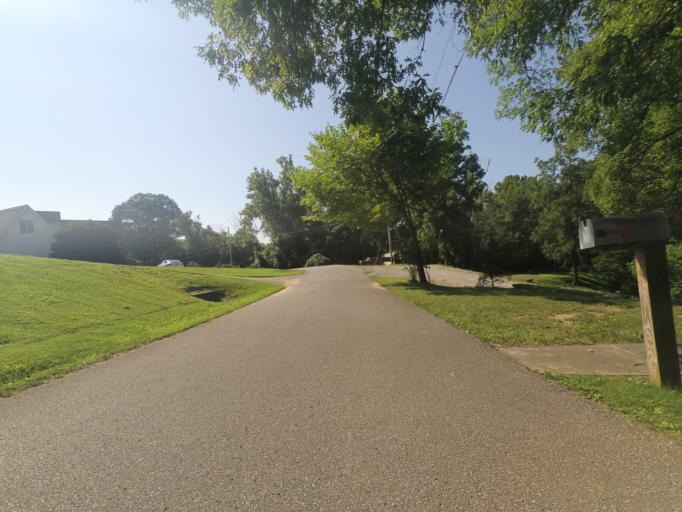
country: US
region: West Virginia
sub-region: Cabell County
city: Huntington
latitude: 38.4312
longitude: -82.4577
